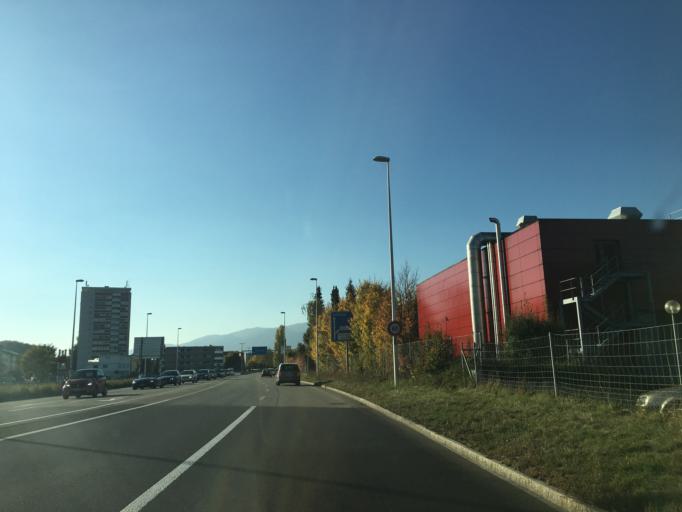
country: CH
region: Solothurn
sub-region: Bezirk Wasseramt
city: Zuchwil
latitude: 47.2035
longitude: 7.5678
